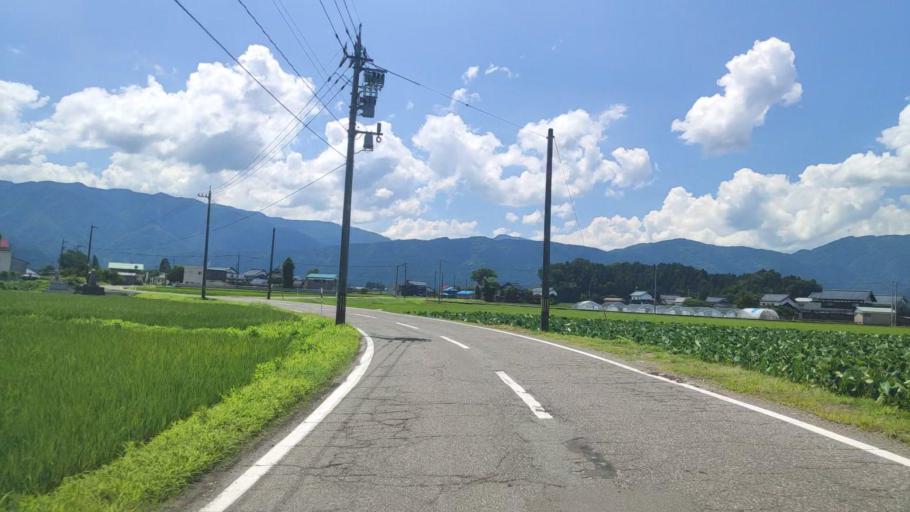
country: JP
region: Fukui
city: Ono
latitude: 35.9728
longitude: 136.5239
